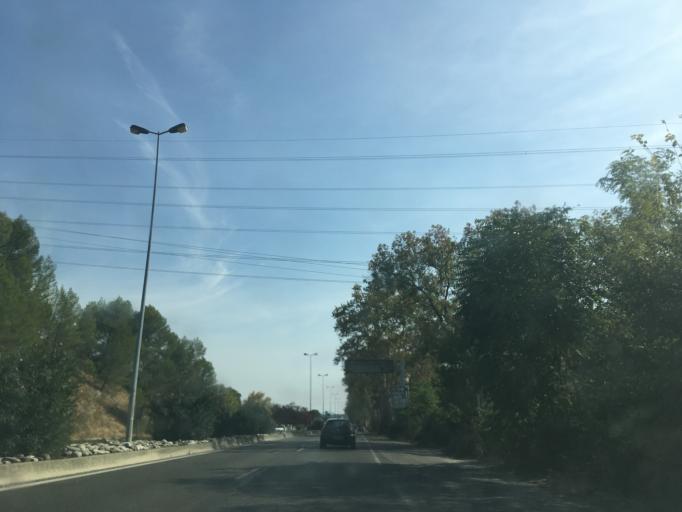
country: FR
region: Provence-Alpes-Cote d'Azur
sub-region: Departement du Var
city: Trans-en-Provence
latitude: 43.5129
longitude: 6.4779
